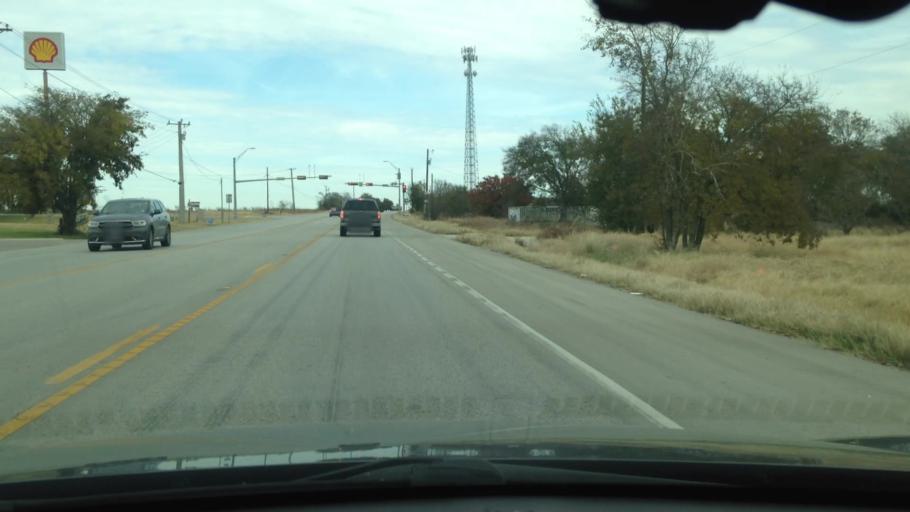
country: US
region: Texas
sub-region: Caldwell County
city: Uhland
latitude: 29.9336
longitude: -97.8194
